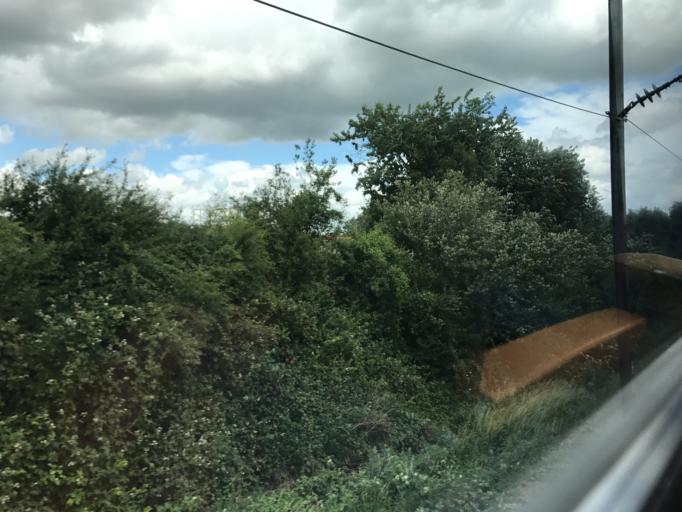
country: LU
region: Luxembourg
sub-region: Canton d'Esch-sur-Alzette
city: Schifflange
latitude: 49.5106
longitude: 6.0269
